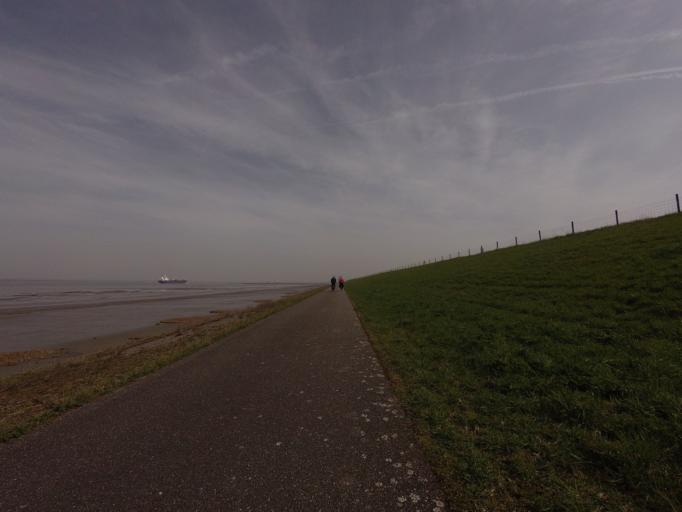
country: NL
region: Zeeland
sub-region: Gemeente Hulst
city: Hulst
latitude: 51.3651
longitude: 4.0636
